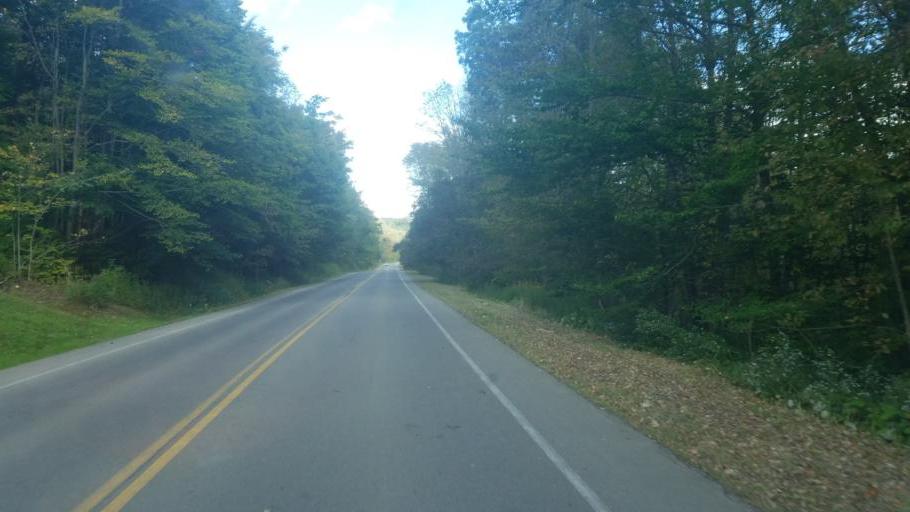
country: US
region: New York
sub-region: Allegany County
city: Cuba
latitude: 42.2257
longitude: -78.3115
